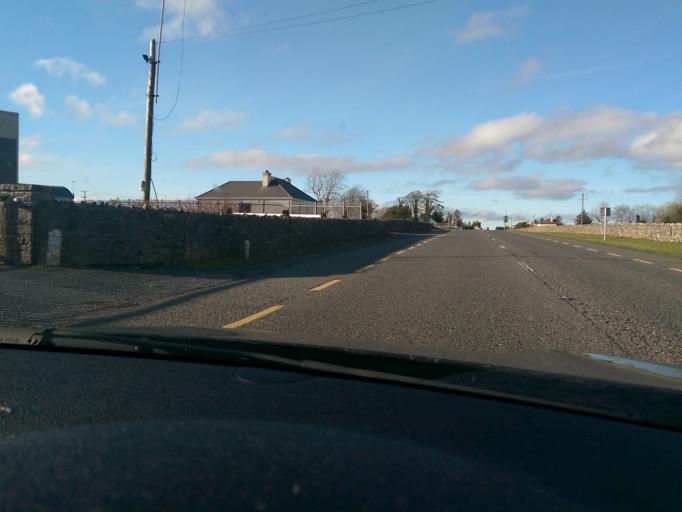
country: IE
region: Connaught
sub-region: Roscommon
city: Roscommon
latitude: 53.6620
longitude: -8.1981
